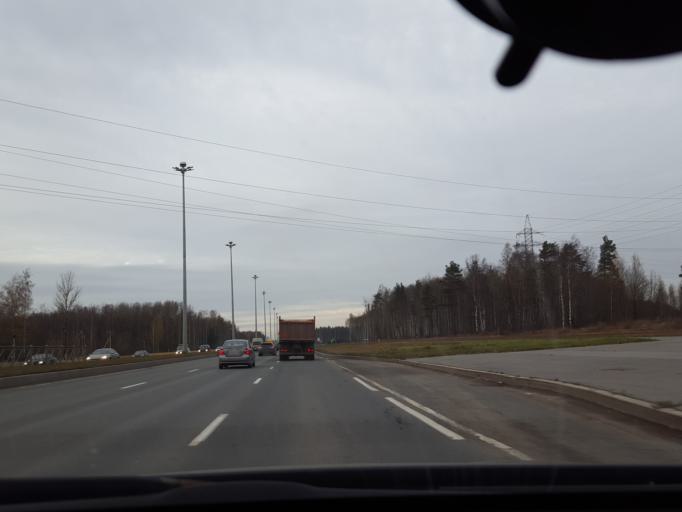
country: RU
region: Leningrad
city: Untolovo
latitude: 60.0451
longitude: 30.2362
